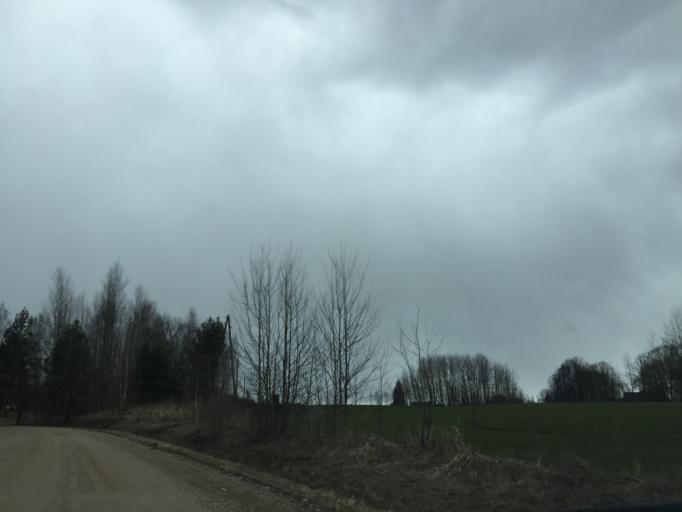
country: LV
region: Varkava
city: Vecvarkava
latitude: 56.0753
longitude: 26.5335
